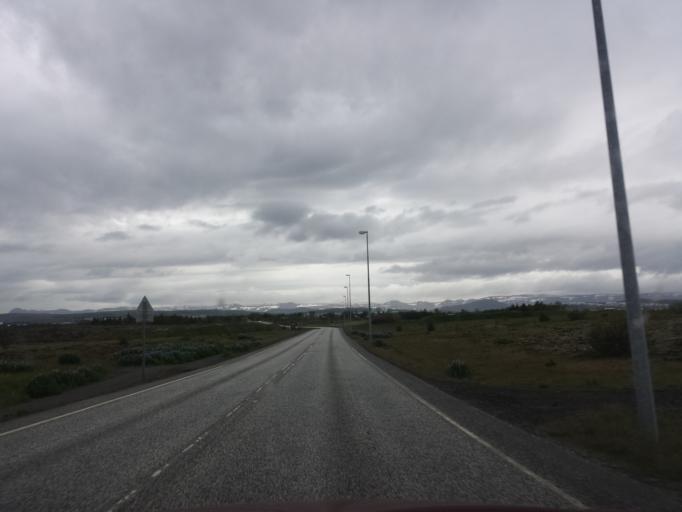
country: IS
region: Capital Region
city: Alftanes
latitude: 64.0882
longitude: -21.9798
